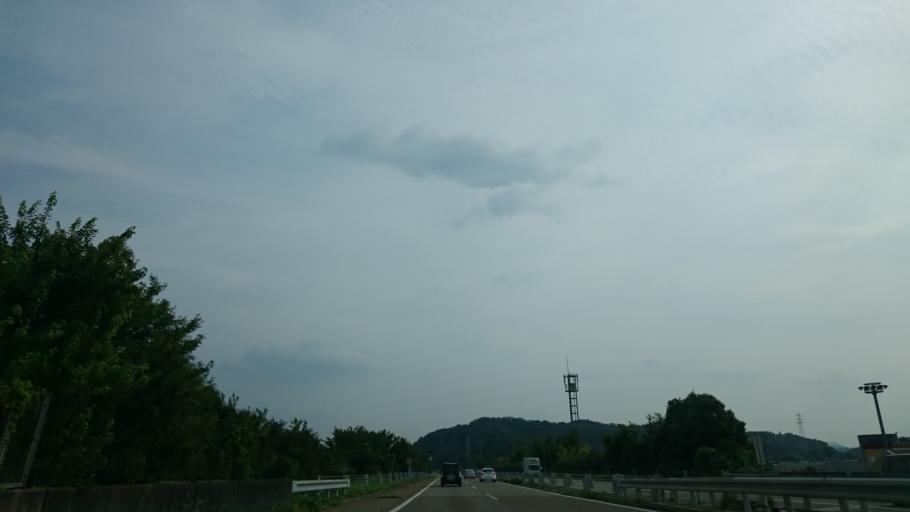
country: JP
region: Gifu
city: Mino
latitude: 35.4981
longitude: 136.8976
